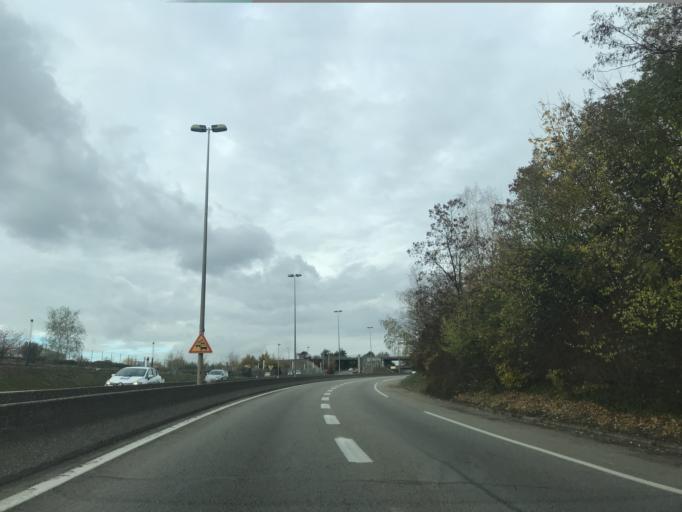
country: FR
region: Rhone-Alpes
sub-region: Departement de la Haute-Savoie
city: Metz-Tessy
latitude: 45.9314
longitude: 6.1191
